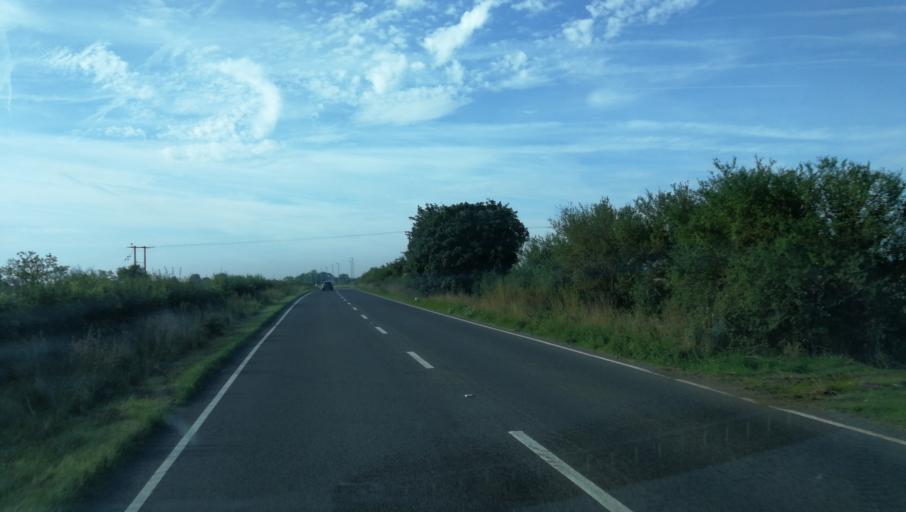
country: GB
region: England
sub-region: Oxfordshire
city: Woodstock
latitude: 51.8761
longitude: -1.3294
